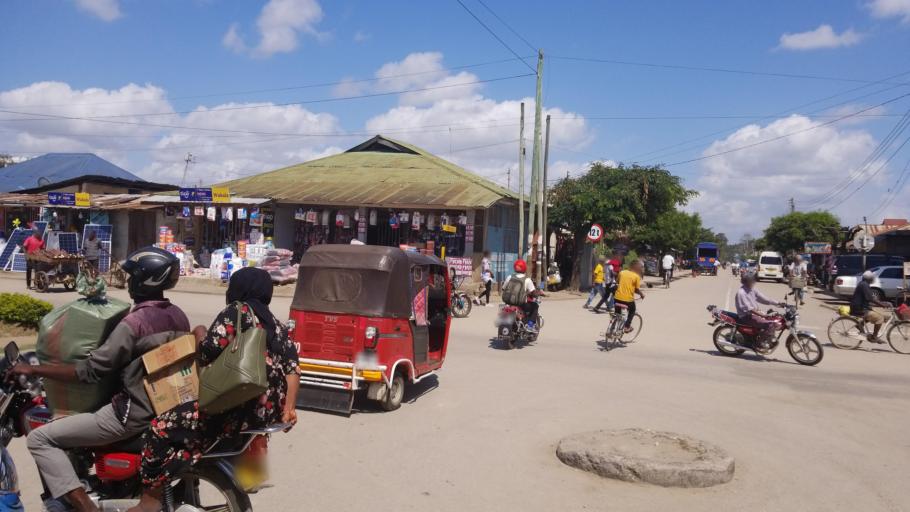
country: TZ
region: Tanga
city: Tanga
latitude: -5.0818
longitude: 39.0979
